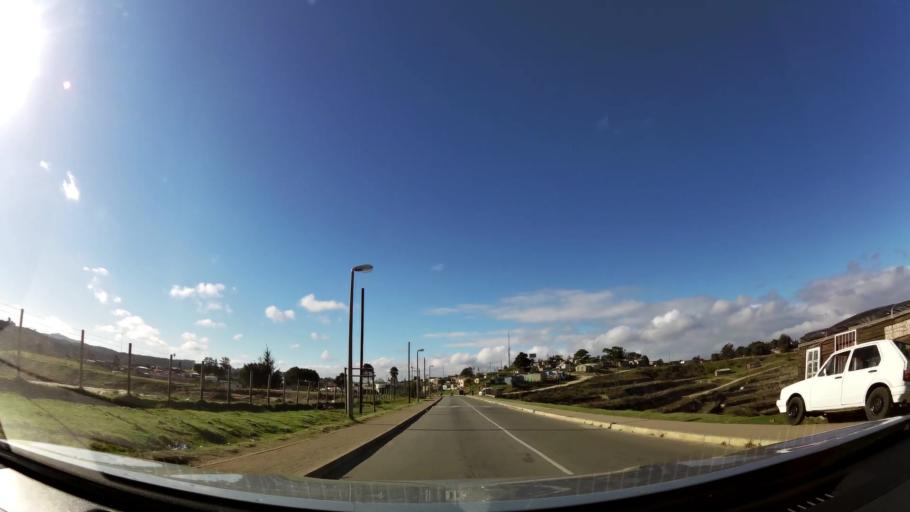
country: ZA
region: Western Cape
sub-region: Eden District Municipality
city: Knysna
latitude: -34.0279
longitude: 23.0679
